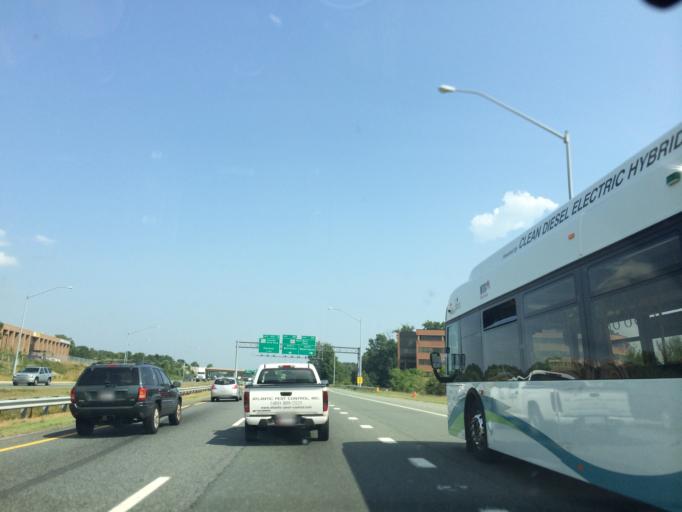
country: US
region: Maryland
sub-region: Howard County
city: Hanover
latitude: 39.1732
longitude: -76.7358
